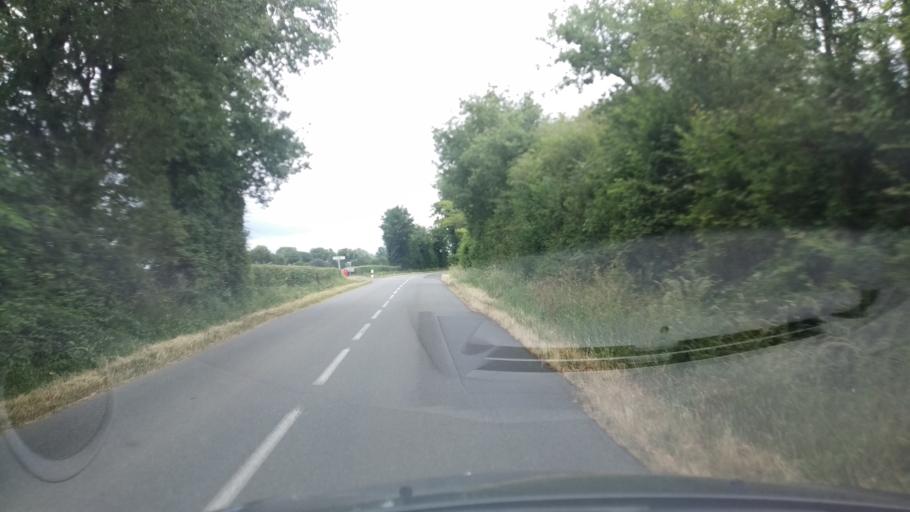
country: FR
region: Poitou-Charentes
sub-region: Departement de la Vienne
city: Vouneuil-sous-Biard
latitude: 46.5616
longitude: 0.2644
